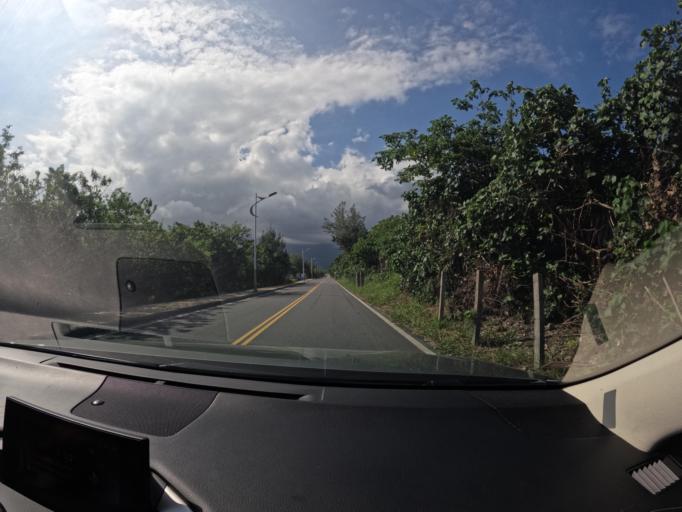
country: TW
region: Taiwan
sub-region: Hualien
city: Hualian
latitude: 24.0189
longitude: 121.6363
